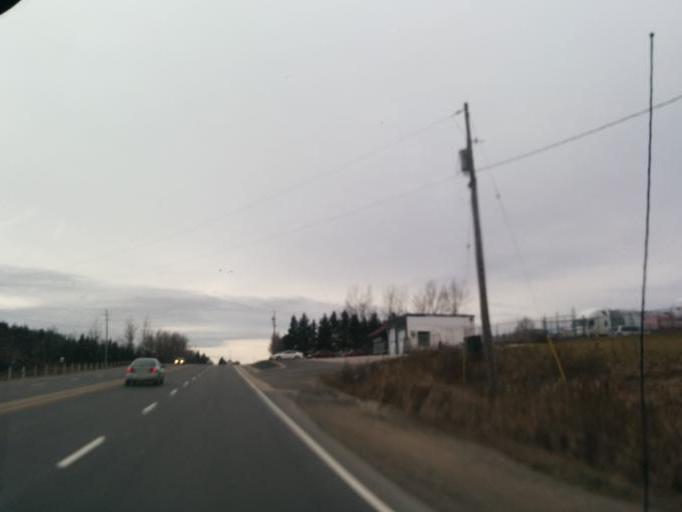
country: CA
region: Ontario
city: Shelburne
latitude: 44.0860
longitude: -80.1637
